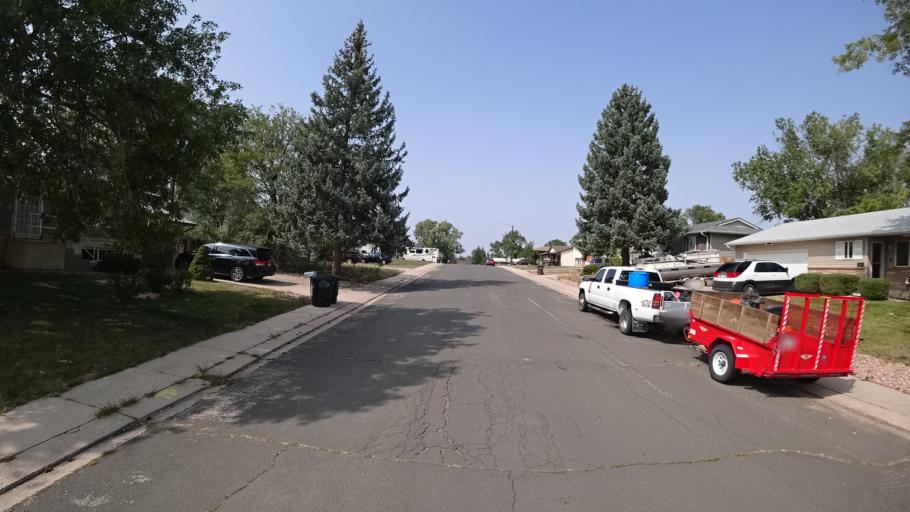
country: US
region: Colorado
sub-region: El Paso County
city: Stratmoor
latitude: 38.8051
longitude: -104.7734
